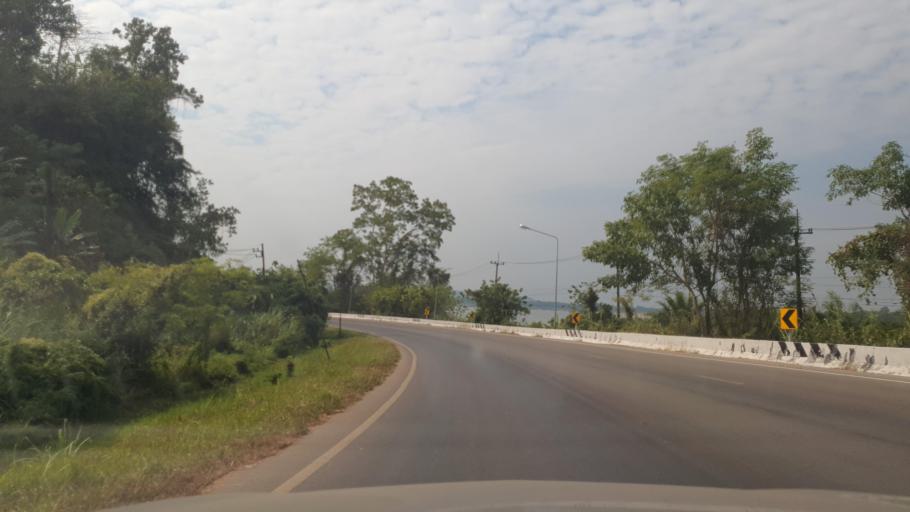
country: TH
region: Changwat Bueng Kan
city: Bung Khla
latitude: 18.2909
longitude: 103.8885
